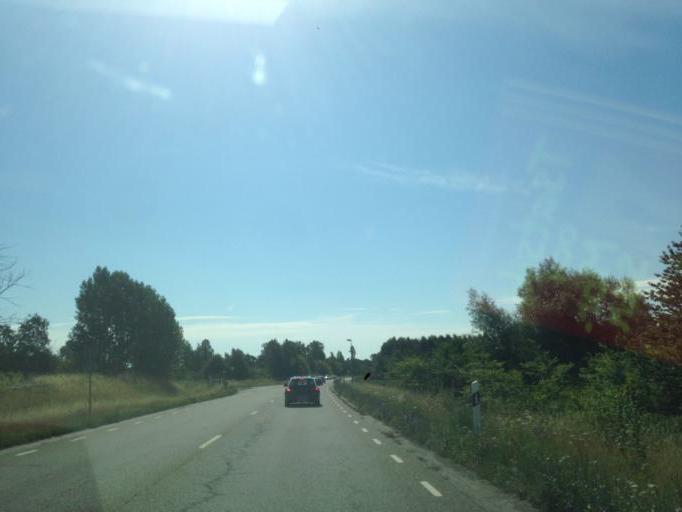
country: SE
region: Skane
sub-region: Simrishamns Kommun
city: Kivik
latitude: 55.6319
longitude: 14.2507
